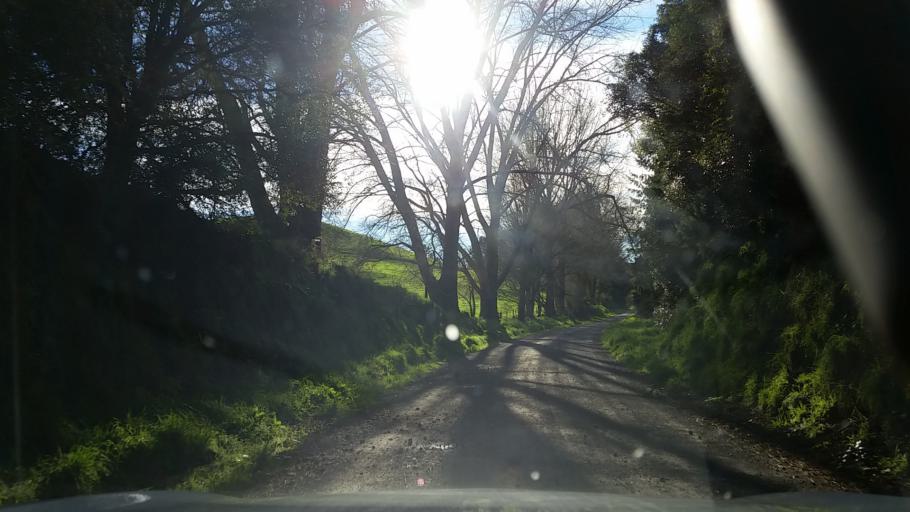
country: NZ
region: Waikato
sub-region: South Waikato District
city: Tokoroa
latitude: -38.3825
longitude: 176.0820
